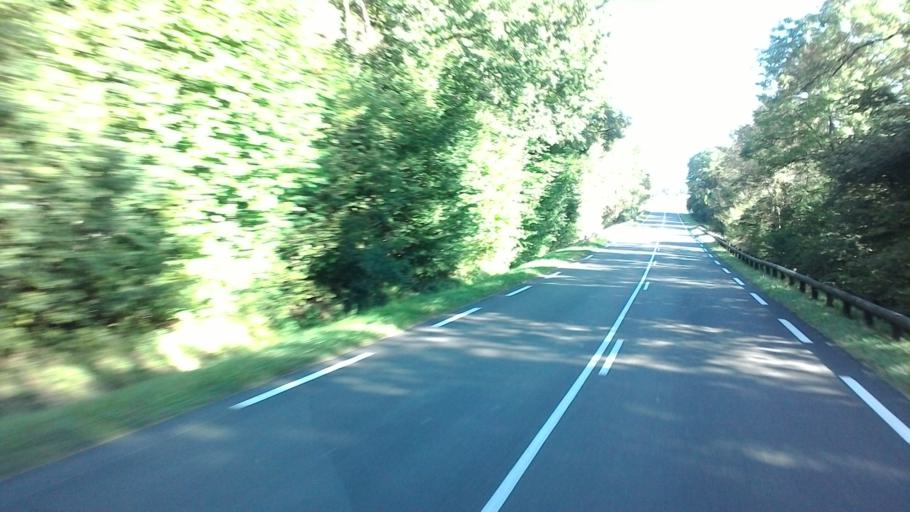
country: FR
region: Bourgogne
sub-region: Departement de la Cote-d'Or
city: Montbard
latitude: 47.7249
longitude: 4.4580
